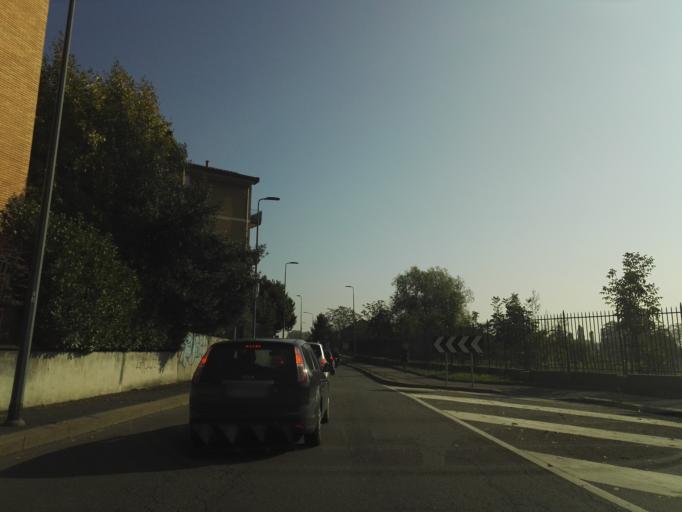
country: IT
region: Lombardy
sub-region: Citta metropolitana di Milano
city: Chiaravalle
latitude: 45.4321
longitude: 9.2227
